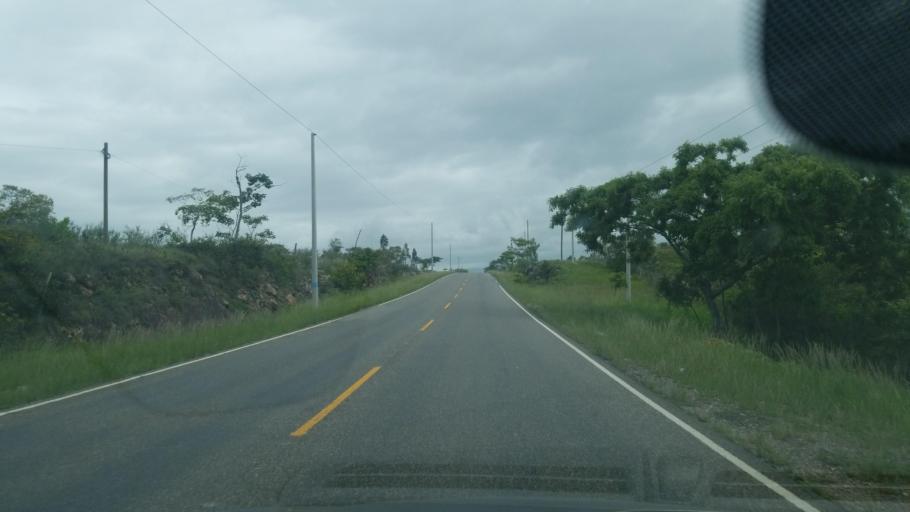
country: HN
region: Ocotepeque
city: Lucerna
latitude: 14.5343
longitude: -88.9491
